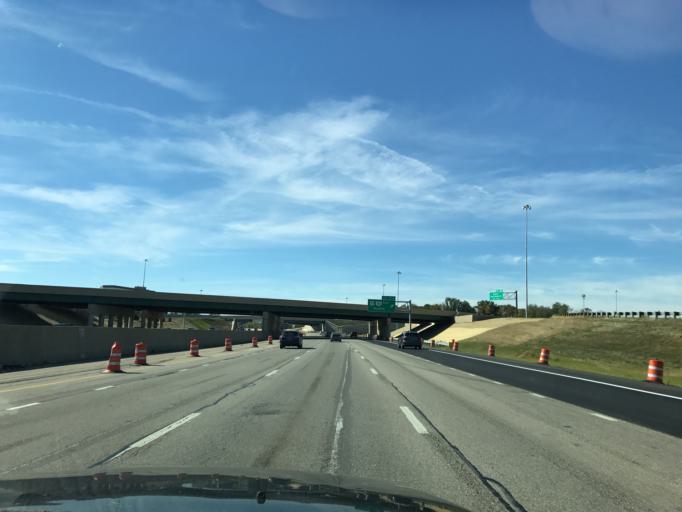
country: US
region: Ohio
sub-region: Franklin County
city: Dublin
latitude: 40.1004
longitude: -83.1334
